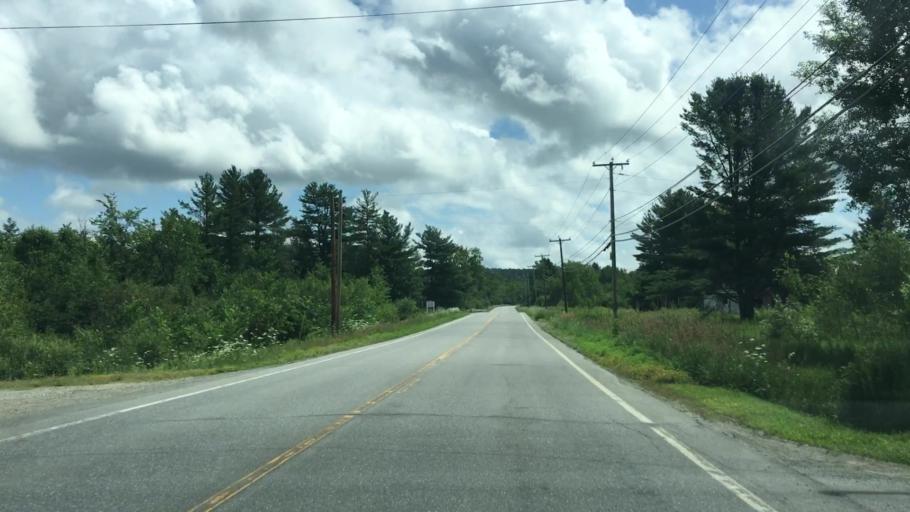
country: US
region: Maine
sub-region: Penobscot County
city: Hermon
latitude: 44.8089
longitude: -68.9772
